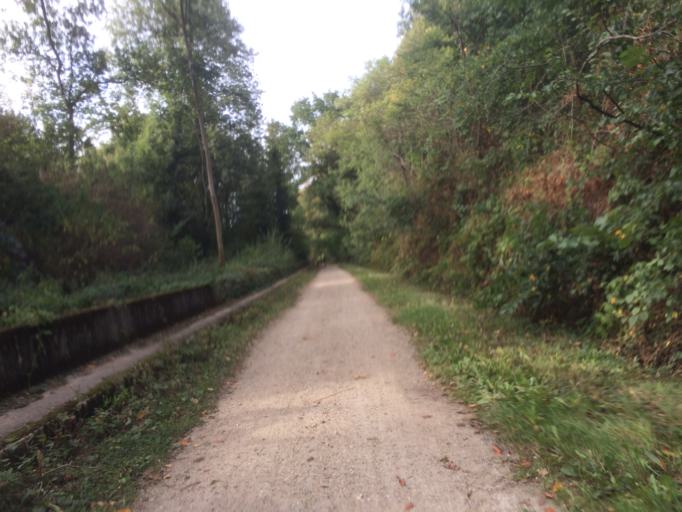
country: FR
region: Ile-de-France
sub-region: Departement de l'Essonne
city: Limours
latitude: 48.6503
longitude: 2.0689
